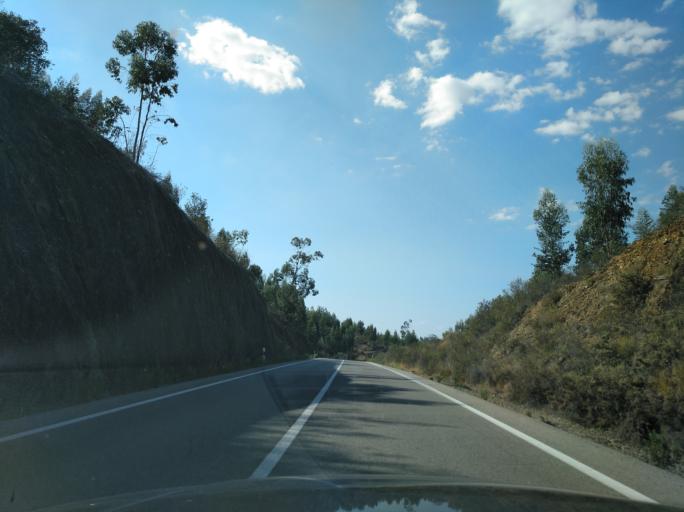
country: ES
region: Andalusia
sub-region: Provincia de Huelva
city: Santa Barbara de Casa
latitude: 37.8133
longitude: -7.2097
